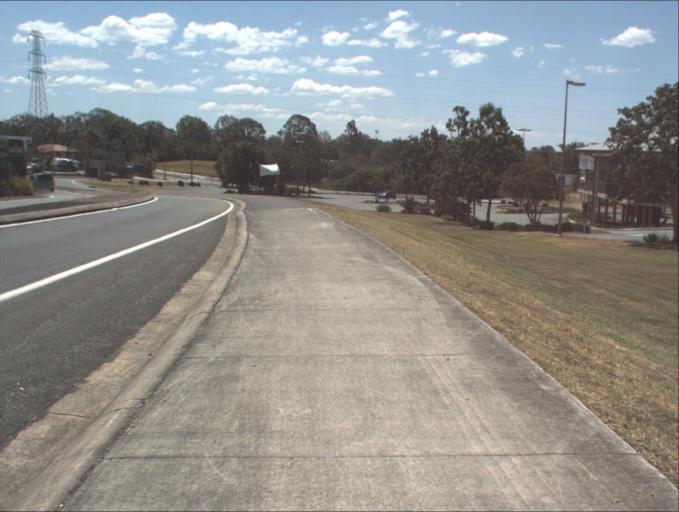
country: AU
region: Queensland
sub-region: Gold Coast
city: Yatala
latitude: -27.7232
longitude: 153.2188
